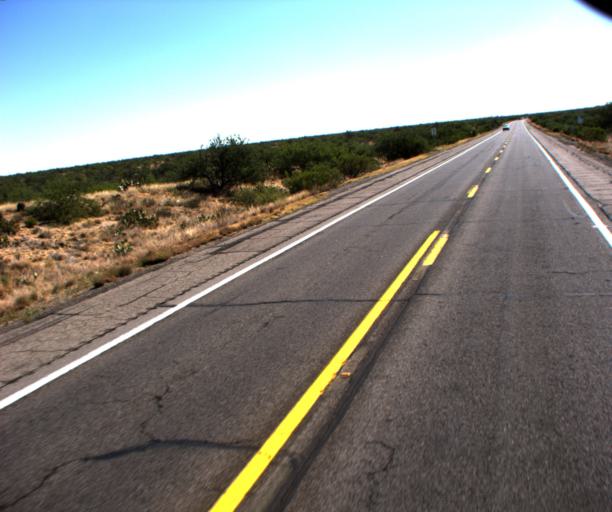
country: US
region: Arizona
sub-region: Pinal County
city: Oracle
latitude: 32.6068
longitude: -110.8562
